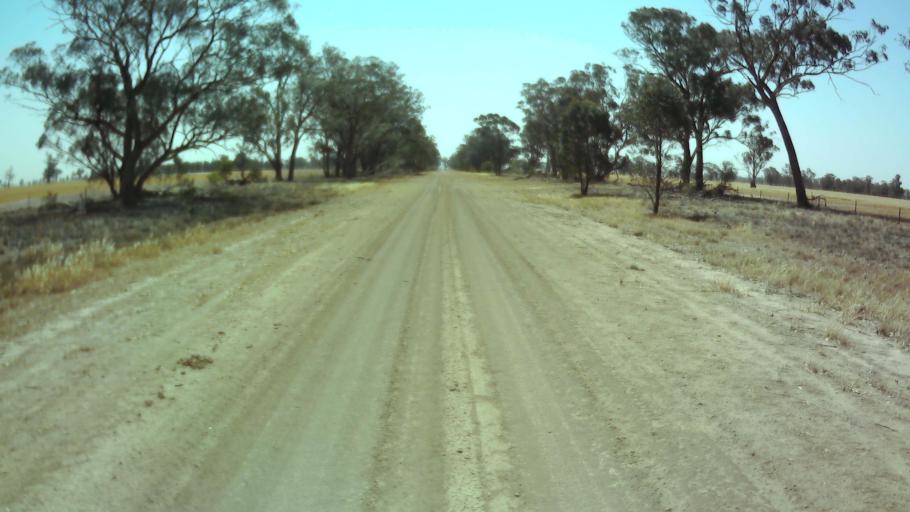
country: AU
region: New South Wales
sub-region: Weddin
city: Grenfell
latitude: -33.9437
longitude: 147.8142
